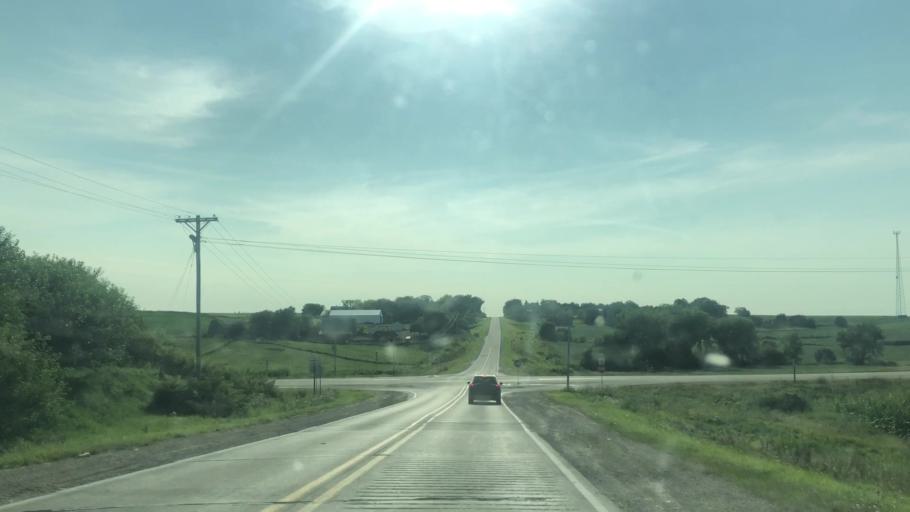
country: US
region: Iowa
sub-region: Marshall County
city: Marshalltown
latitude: 42.0488
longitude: -92.9990
